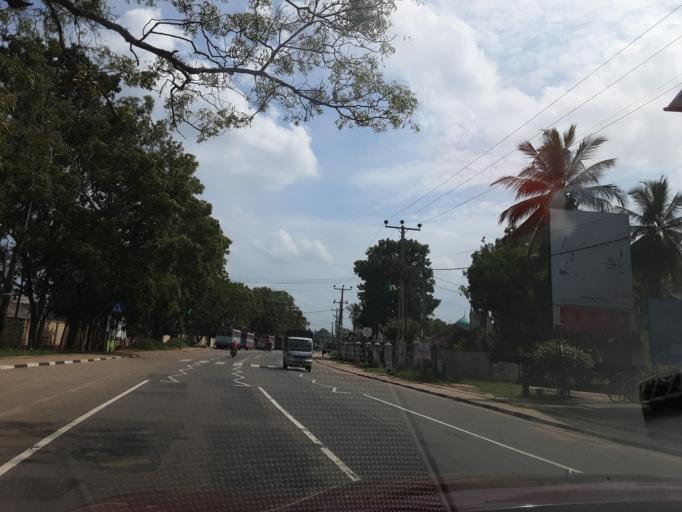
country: LK
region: Northern Province
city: Vavuniya
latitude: 8.5357
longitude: 80.4946
